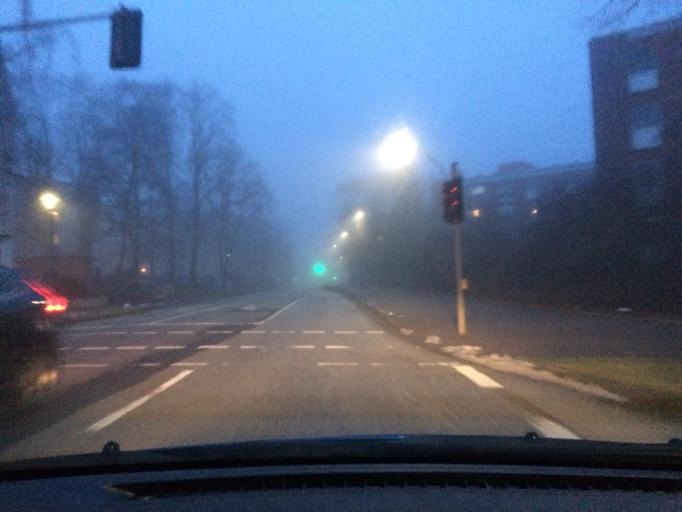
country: DE
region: Schleswig-Holstein
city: Geesthacht
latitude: 53.4396
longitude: 10.3911
